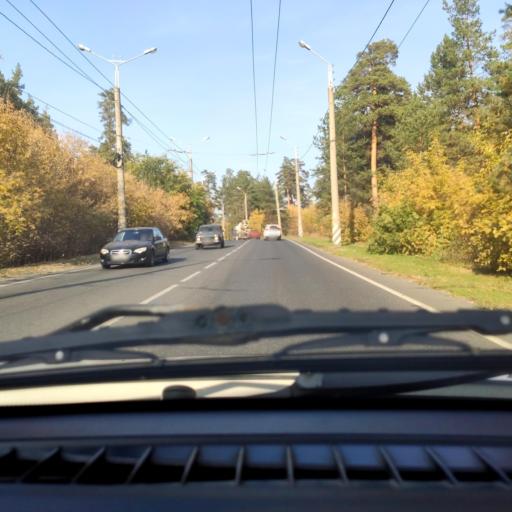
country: RU
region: Samara
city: Tol'yatti
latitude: 53.4770
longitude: 49.3493
